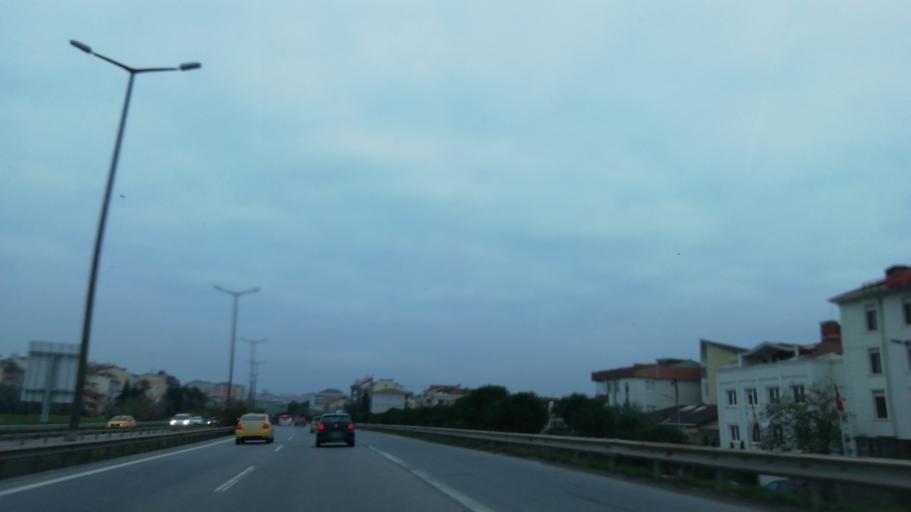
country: TR
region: Istanbul
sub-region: Atasehir
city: Atasehir
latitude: 41.0063
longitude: 29.0767
